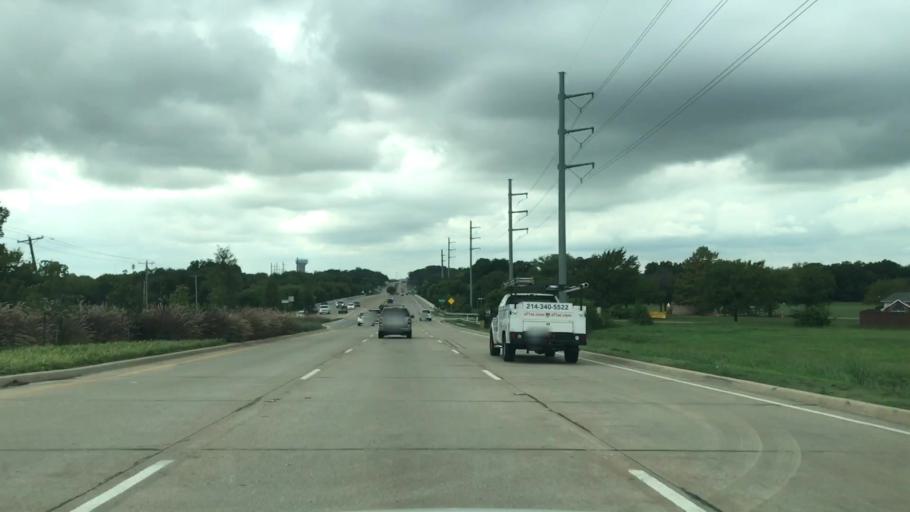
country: US
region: Texas
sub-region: Dallas County
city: Rowlett
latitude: 32.9091
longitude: -96.5879
